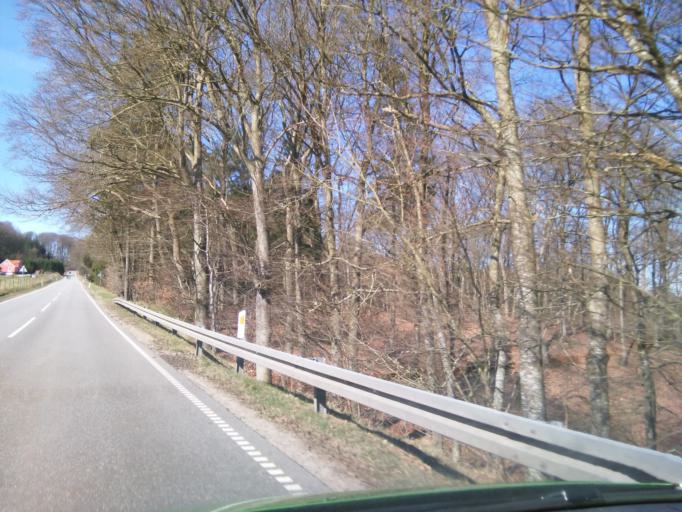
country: DK
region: Central Jutland
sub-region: Horsens Kommune
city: Braedstrup
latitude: 56.0151
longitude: 9.6692
